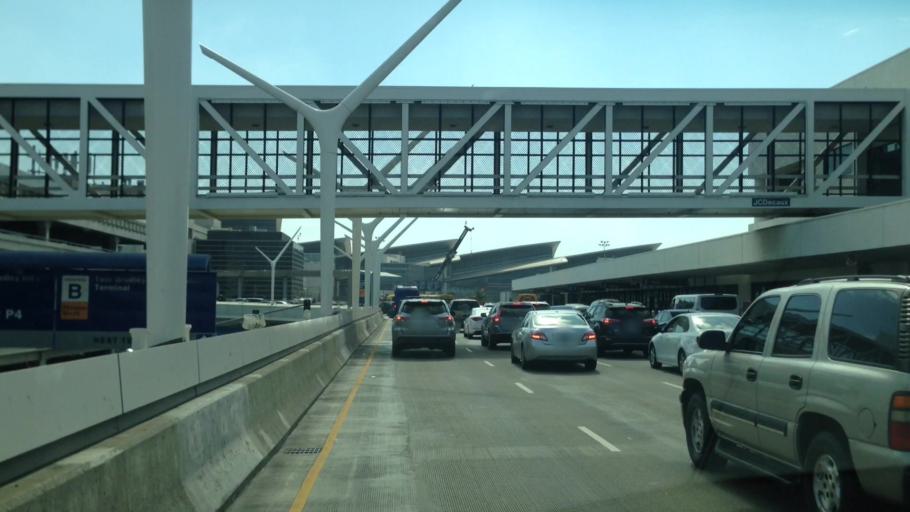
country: US
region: California
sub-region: Los Angeles County
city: El Segundo
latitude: 33.9449
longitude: -118.4069
